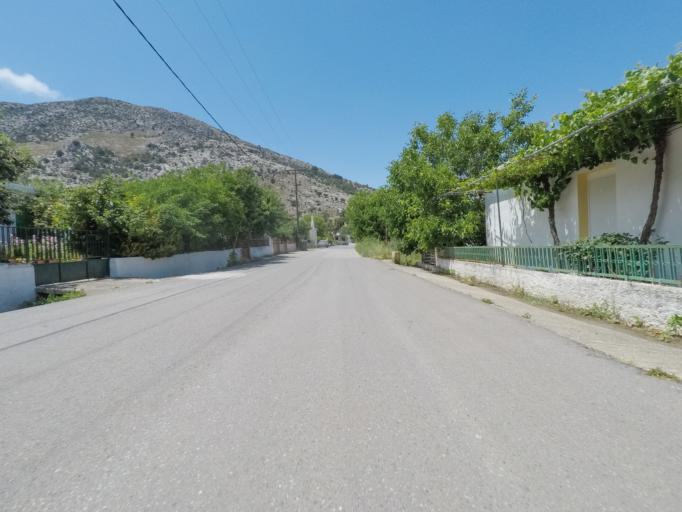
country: GR
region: Crete
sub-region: Nomos Irakleiou
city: Mokhos
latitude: 35.1840
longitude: 25.4328
